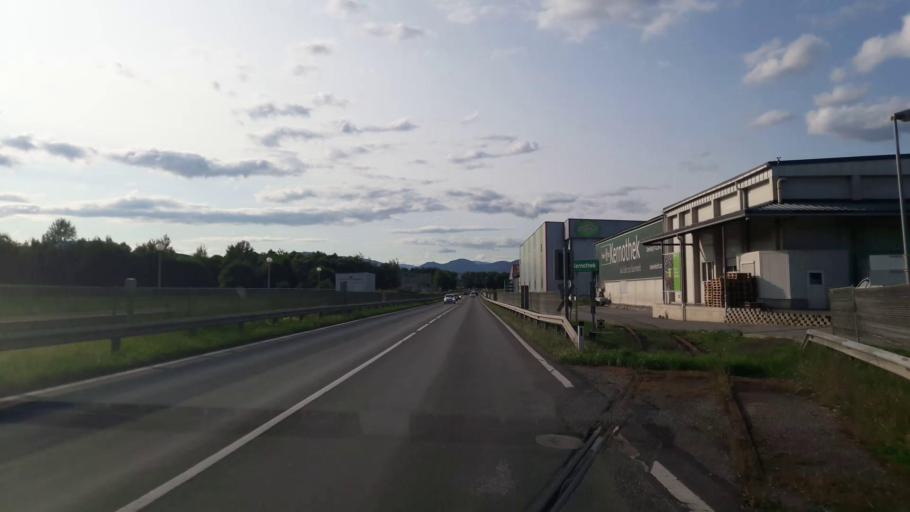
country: AT
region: Styria
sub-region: Politischer Bezirk Weiz
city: Sankt Ruprecht an der Raab
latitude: 47.1344
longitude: 15.6825
